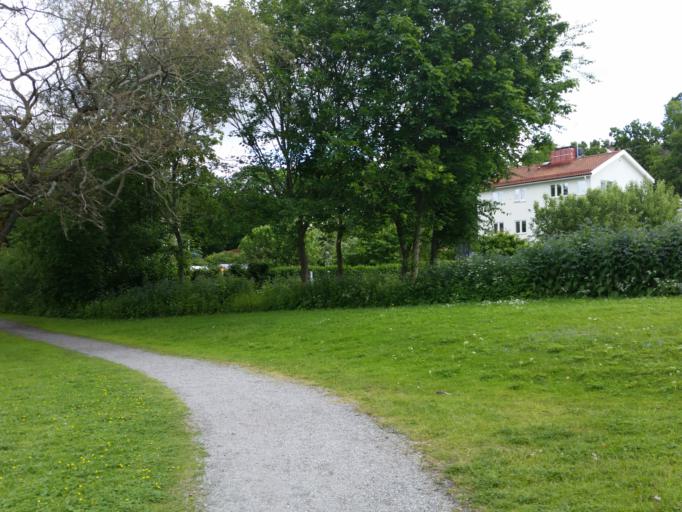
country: SE
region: Stockholm
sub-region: Solna Kommun
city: Rasunda
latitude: 59.3698
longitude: 17.9918
